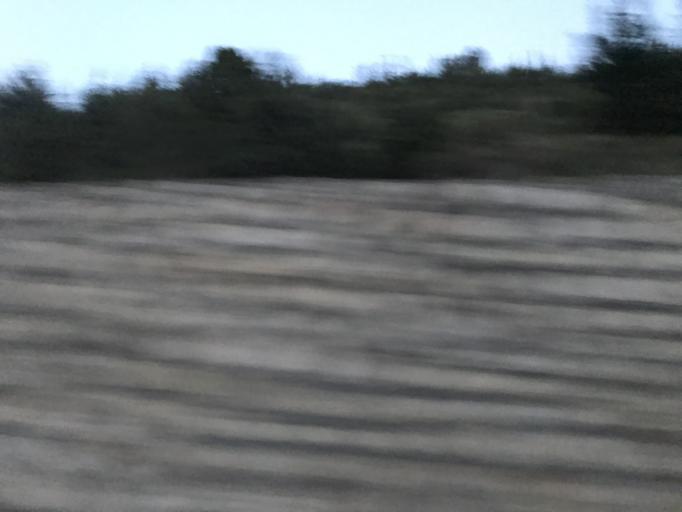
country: TR
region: Hatay
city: Karacay
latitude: 36.1587
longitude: 36.0970
